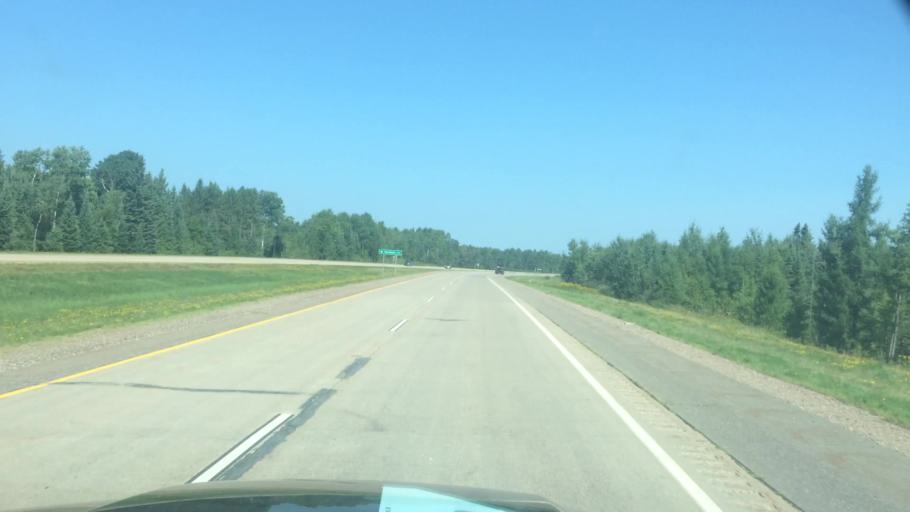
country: US
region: Wisconsin
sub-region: Lincoln County
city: Tomahawk
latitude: 45.3784
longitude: -89.6690
